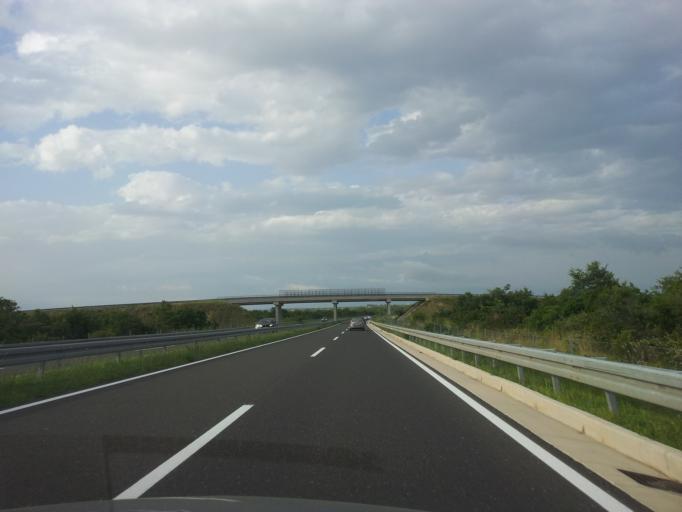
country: HR
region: Zadarska
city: Galovac
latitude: 44.0816
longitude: 15.3524
